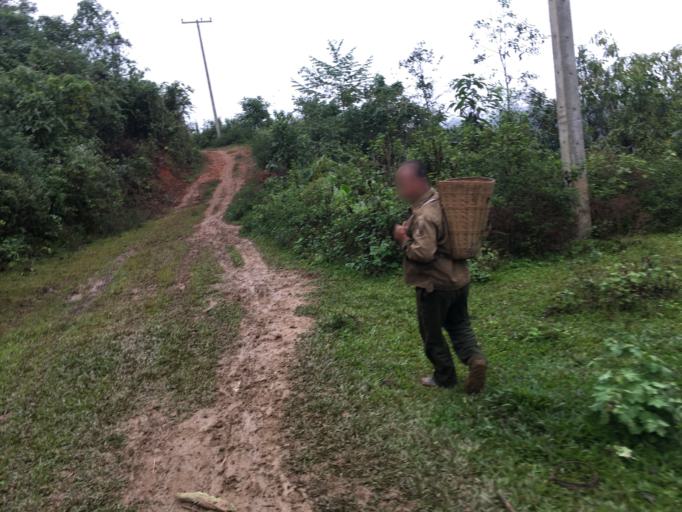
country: LA
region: Houaphan
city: Xamtay
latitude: 19.8971
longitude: 104.4605
